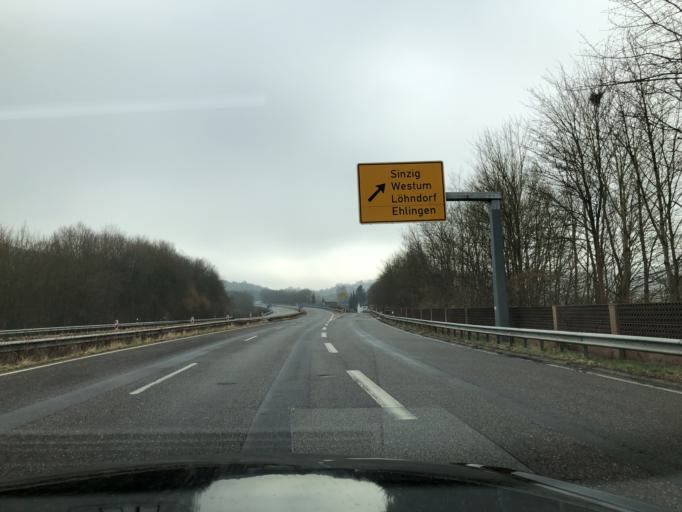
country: DE
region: Rheinland-Pfalz
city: Remagen
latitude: 50.5466
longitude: 7.1975
